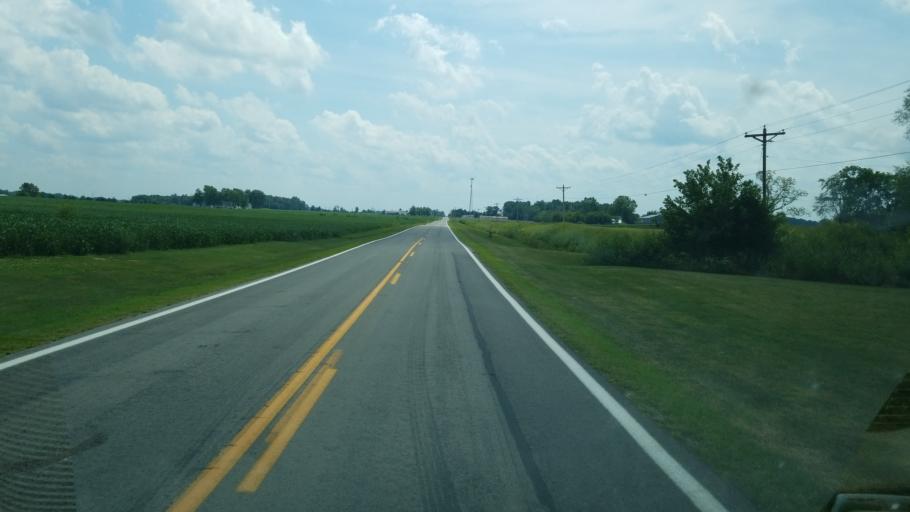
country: US
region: Ohio
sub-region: Hancock County
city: Arlington
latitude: 40.9562
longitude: -83.7274
